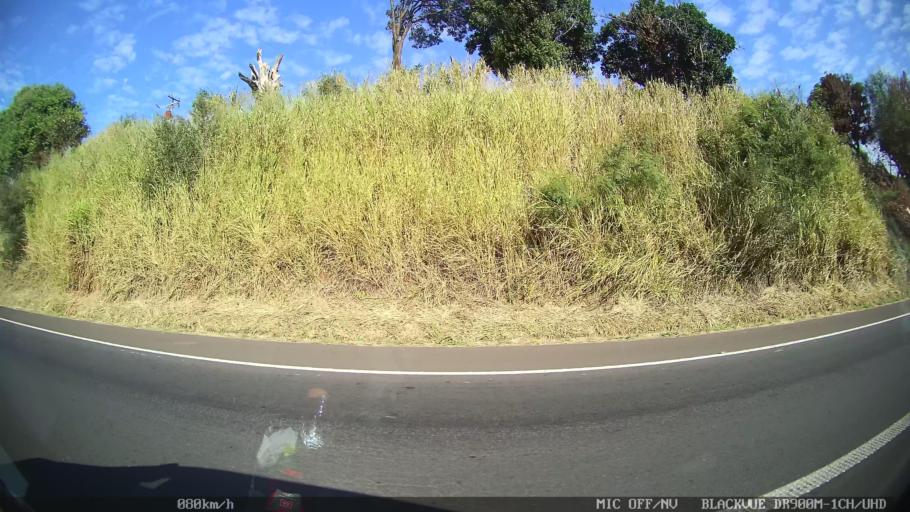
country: BR
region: Sao Paulo
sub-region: Americana
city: Americana
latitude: -22.7579
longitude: -47.3137
